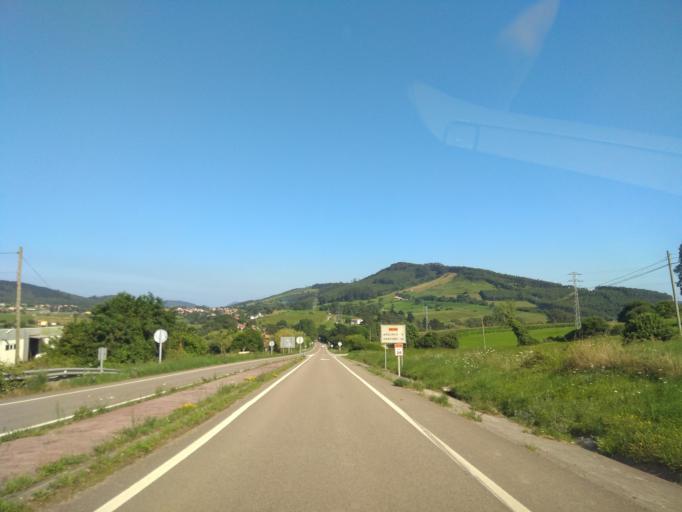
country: ES
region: Cantabria
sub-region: Provincia de Cantabria
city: Bareyo
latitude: 43.4733
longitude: -3.5936
